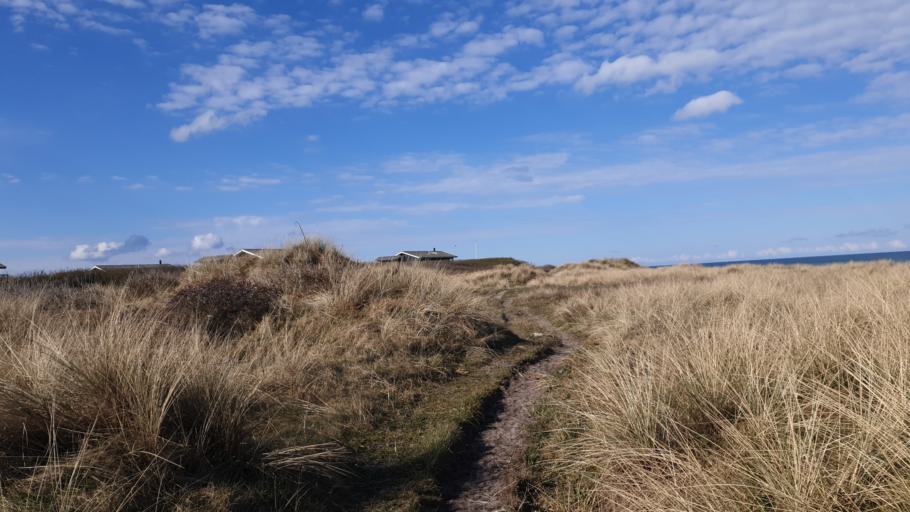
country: DK
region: North Denmark
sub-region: Hjorring Kommune
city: Hjorring
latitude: 57.4957
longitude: 9.8341
